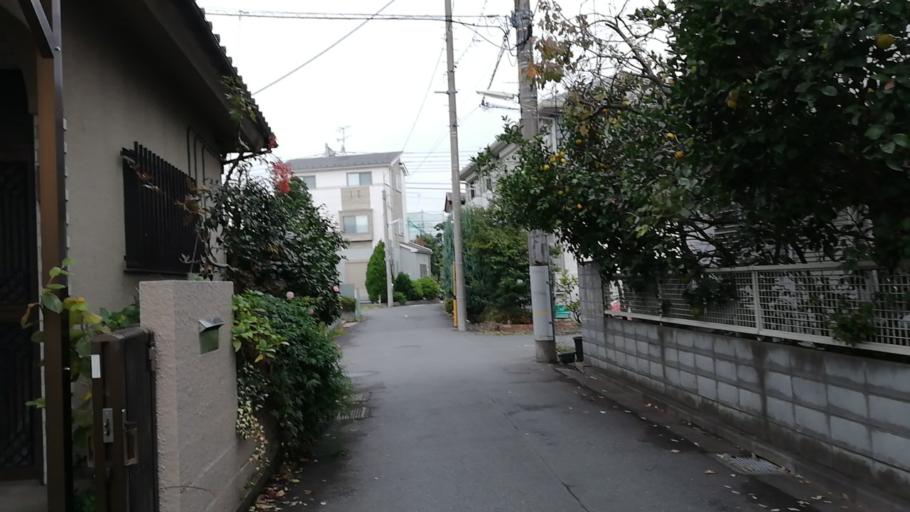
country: JP
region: Tokyo
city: Chofugaoka
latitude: 35.6513
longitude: 139.5683
